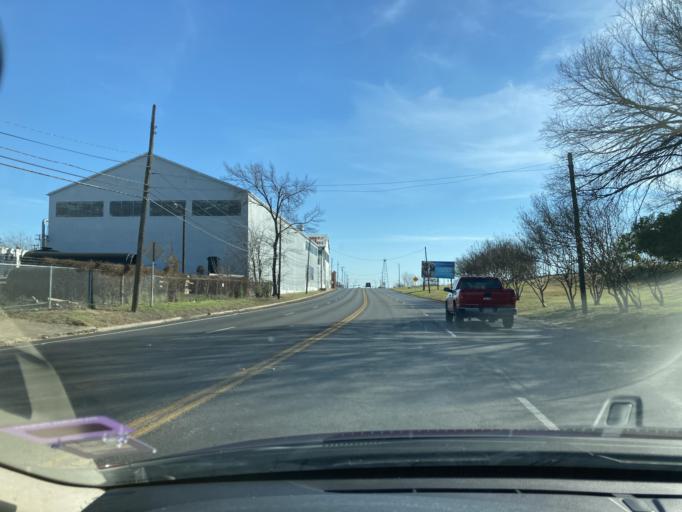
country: US
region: Texas
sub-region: Navarro County
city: Corsicana
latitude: 32.0995
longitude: -96.4632
